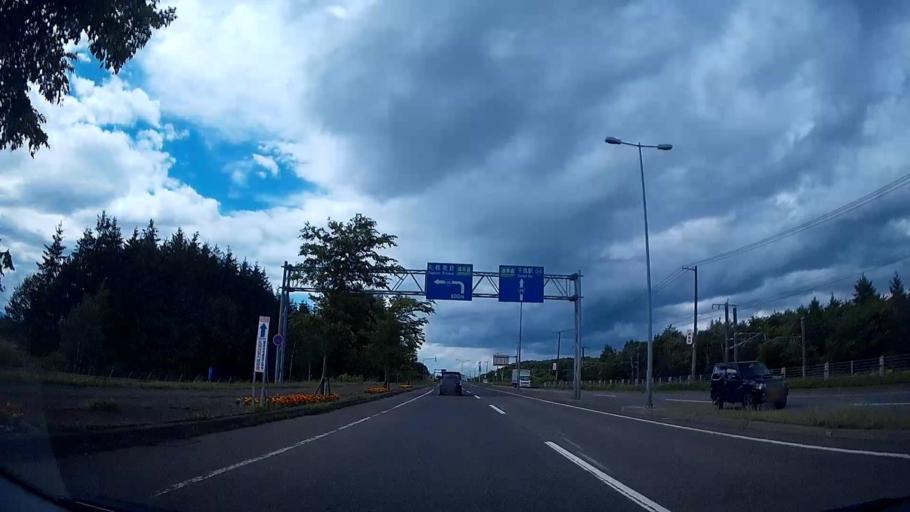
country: JP
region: Hokkaido
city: Chitose
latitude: 42.8143
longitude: 141.6674
